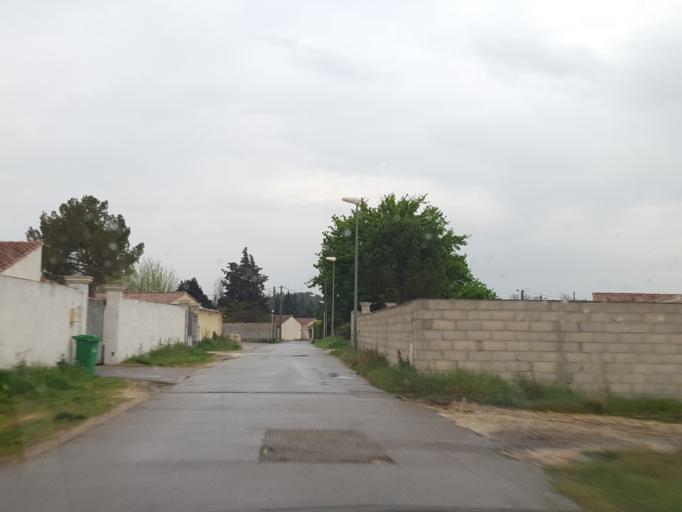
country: FR
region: Provence-Alpes-Cote d'Azur
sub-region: Departement du Vaucluse
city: Saint-Saturnin-les-Avignon
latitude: 43.9661
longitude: 4.9273
